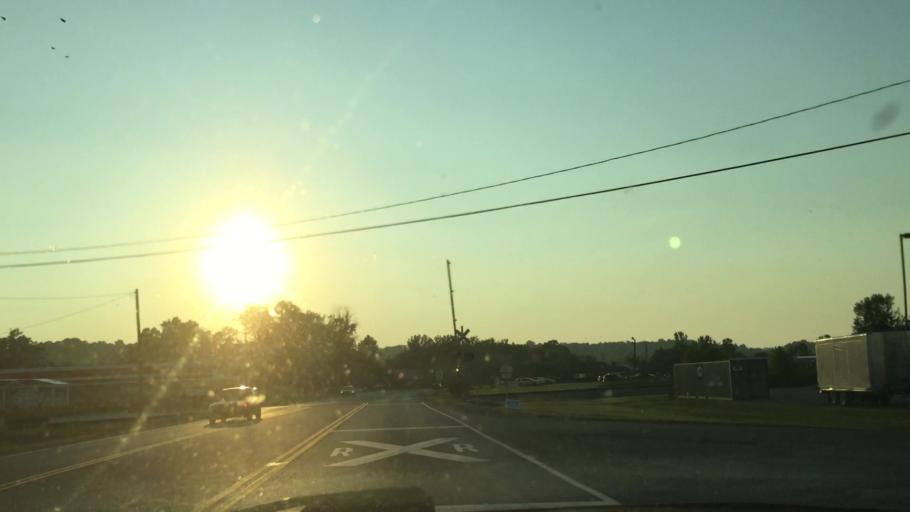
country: US
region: Kentucky
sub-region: Carroll County
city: Carrollton
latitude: 38.6574
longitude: -85.1342
